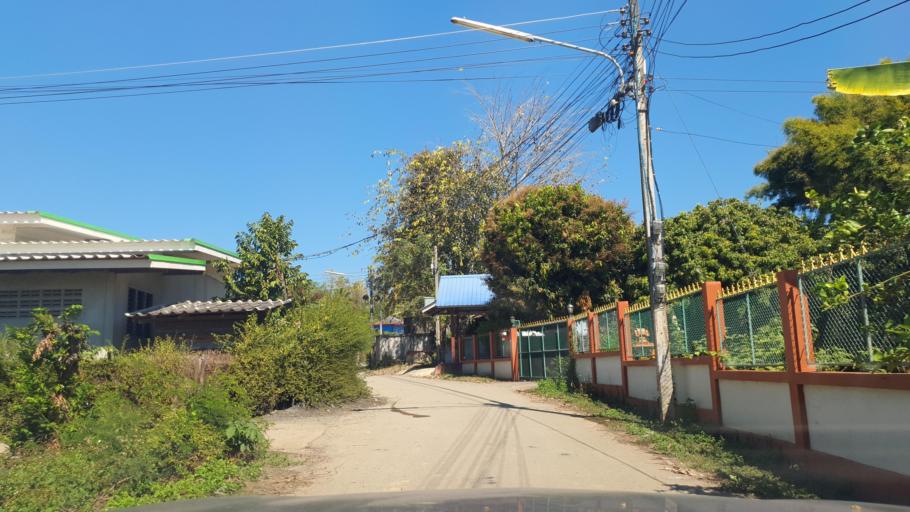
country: TH
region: Chiang Mai
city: Mae Wang
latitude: 18.6783
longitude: 98.8185
